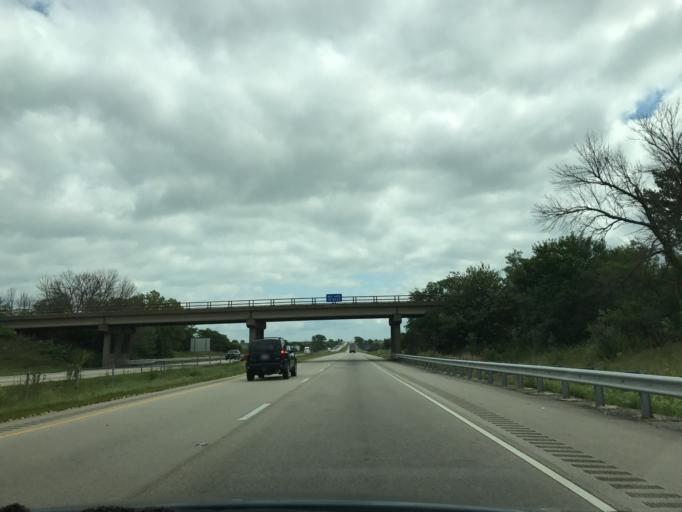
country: US
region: Illinois
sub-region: LaSalle County
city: Marseilles
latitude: 41.3753
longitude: -88.7462
